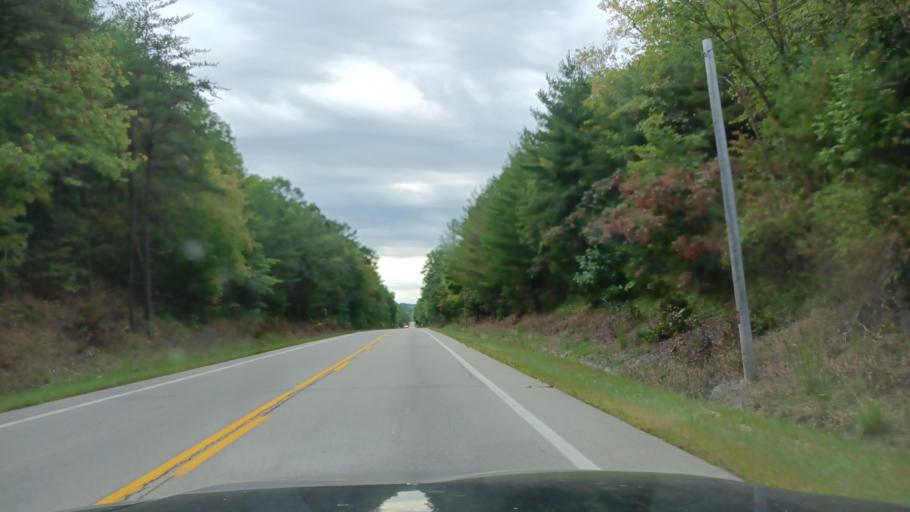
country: US
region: Ohio
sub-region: Vinton County
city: McArthur
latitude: 39.2389
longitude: -82.3978
